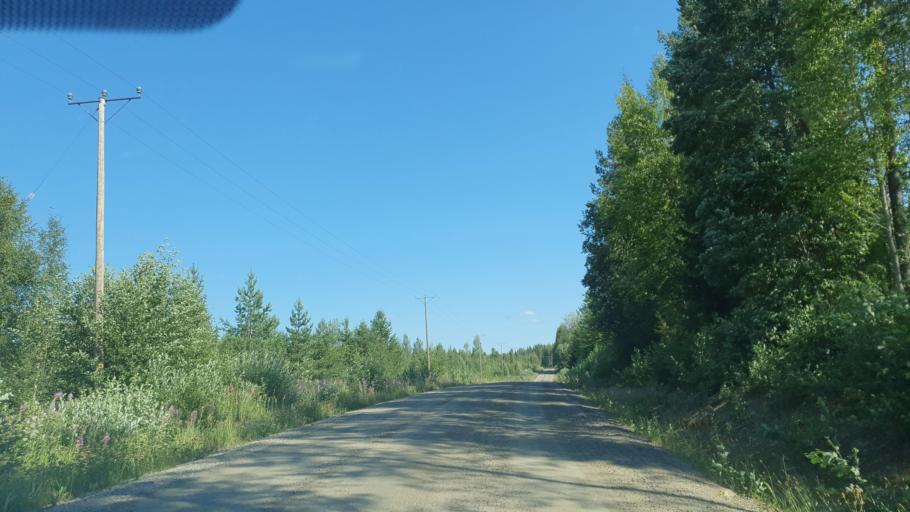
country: FI
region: Kainuu
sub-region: Kehys-Kainuu
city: Kuhmo
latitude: 64.0496
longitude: 29.6146
